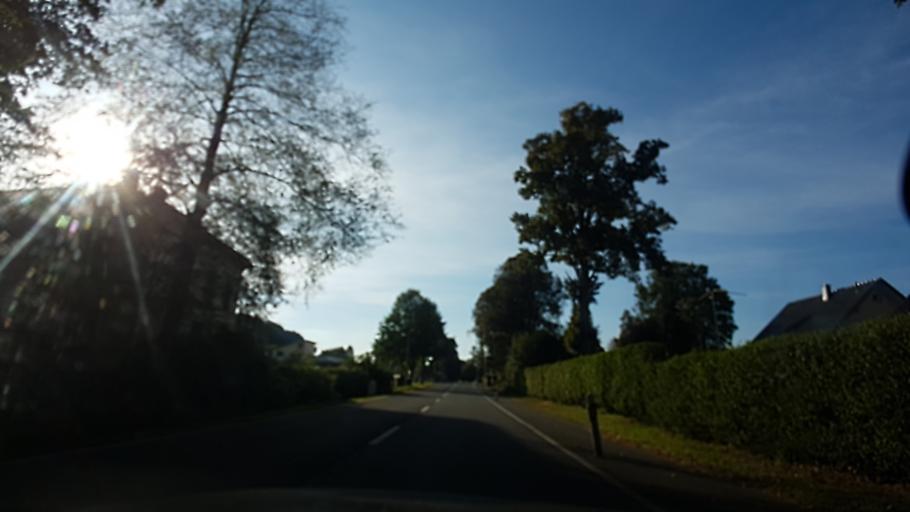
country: DE
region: North Rhine-Westphalia
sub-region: Regierungsbezirk Koln
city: Marienheide
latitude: 51.1119
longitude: 7.5018
